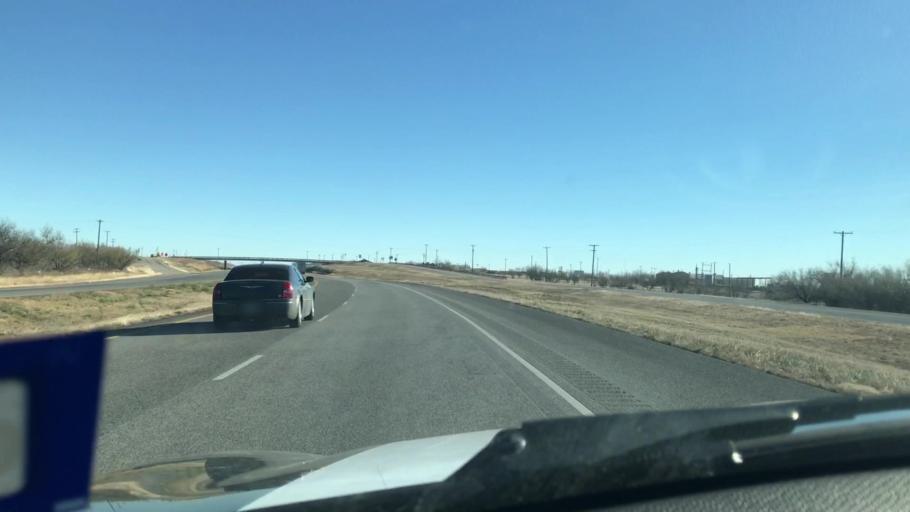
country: US
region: Texas
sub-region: Scurry County
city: Snyder
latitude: 32.7959
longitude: -100.9636
